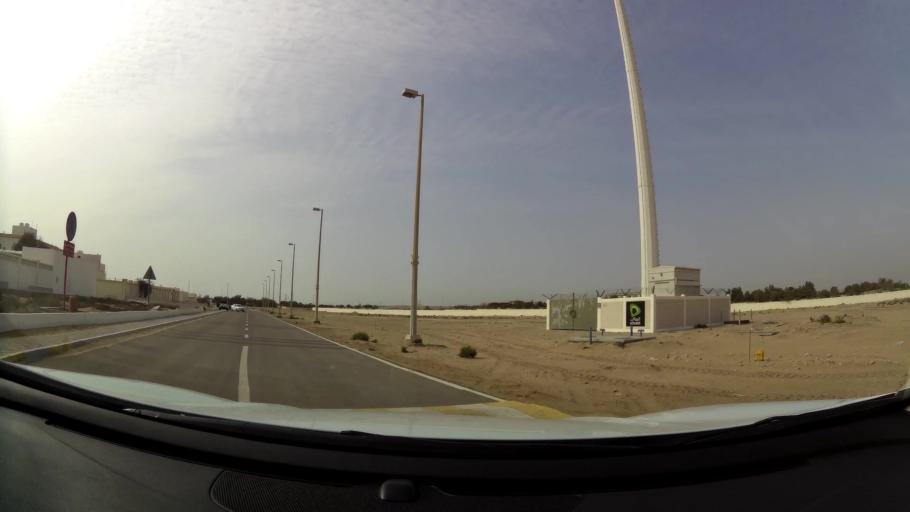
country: AE
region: Abu Dhabi
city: Abu Dhabi
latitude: 24.6169
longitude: 54.7062
